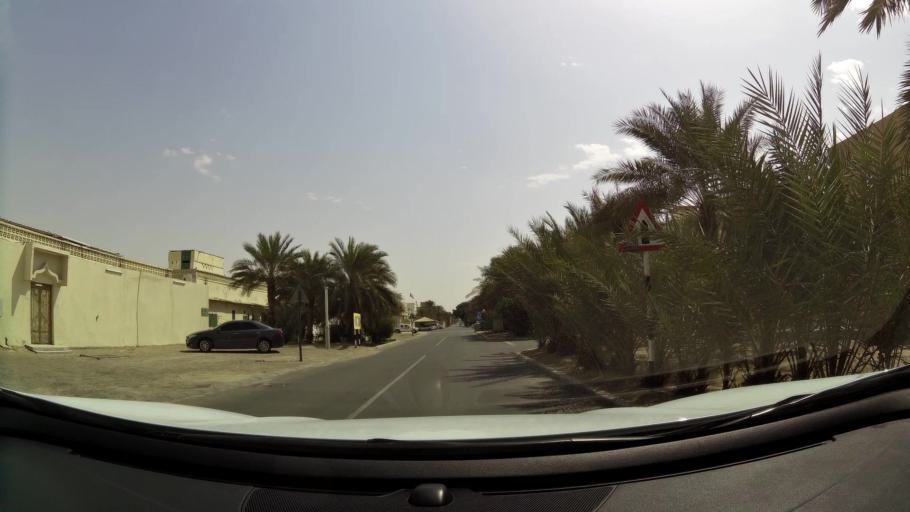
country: AE
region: Abu Dhabi
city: Abu Dhabi
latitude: 24.2966
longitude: 54.6310
